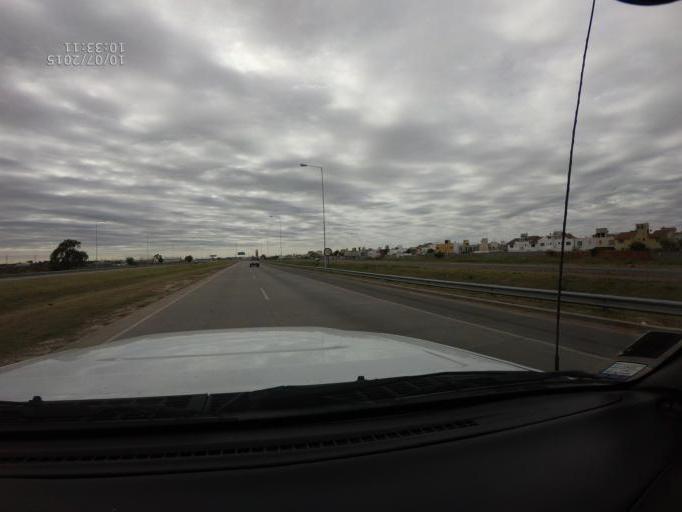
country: AR
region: Cordoba
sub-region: Departamento de Capital
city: Cordoba
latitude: -31.3546
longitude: -64.2174
